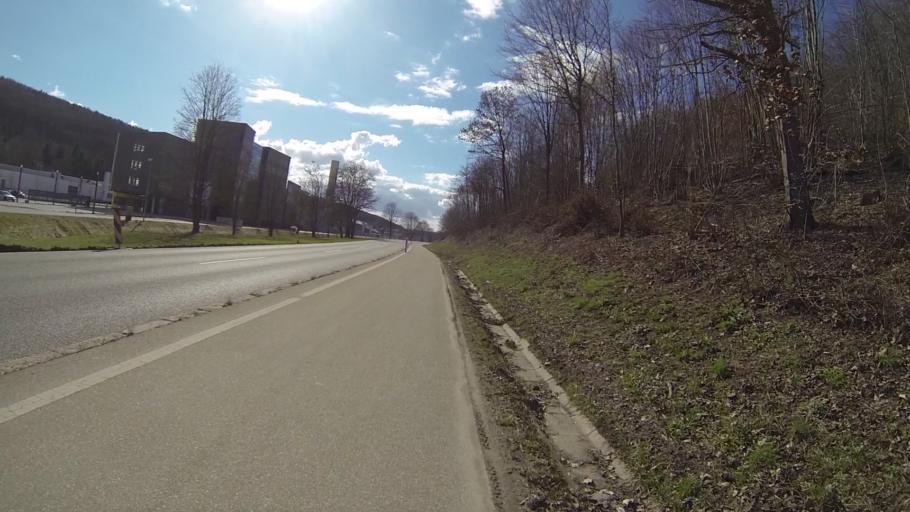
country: DE
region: Baden-Wuerttemberg
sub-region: Regierungsbezirk Stuttgart
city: Heidenheim an der Brenz
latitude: 48.6799
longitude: 10.1177
